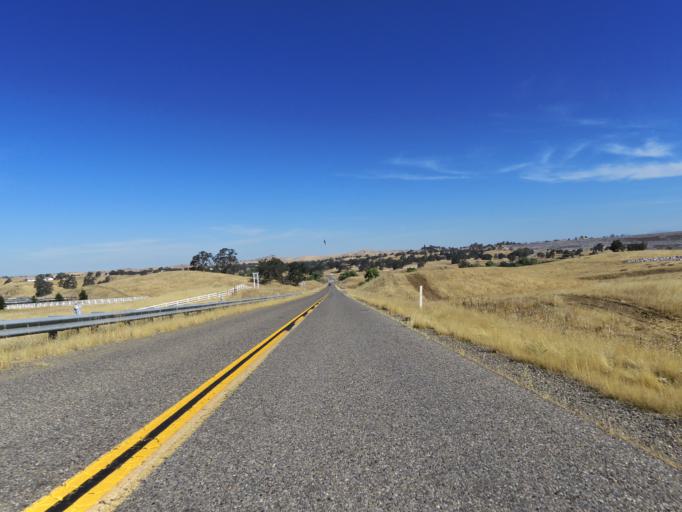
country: US
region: California
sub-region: Madera County
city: Bonadelle Ranchos-Madera Ranchos
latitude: 37.1007
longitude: -119.8829
